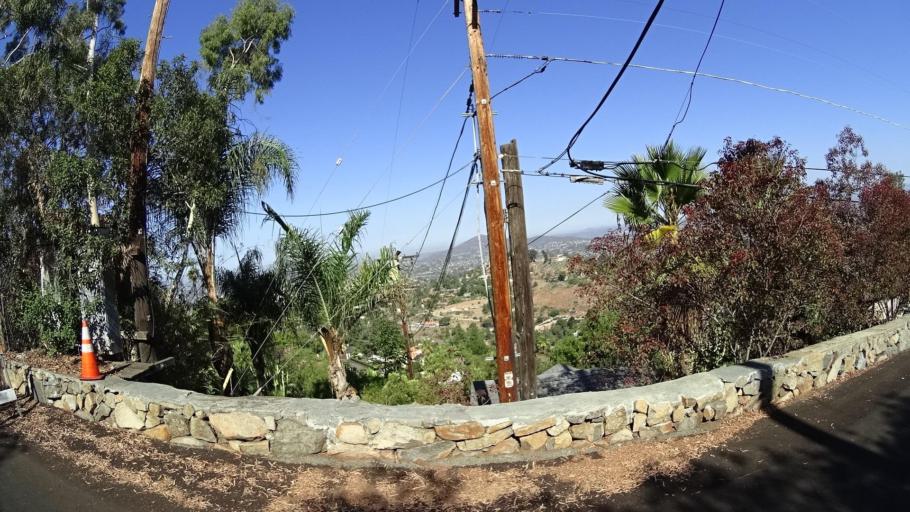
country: US
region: California
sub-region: San Diego County
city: Casa de Oro-Mount Helix
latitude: 32.7675
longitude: -116.9842
